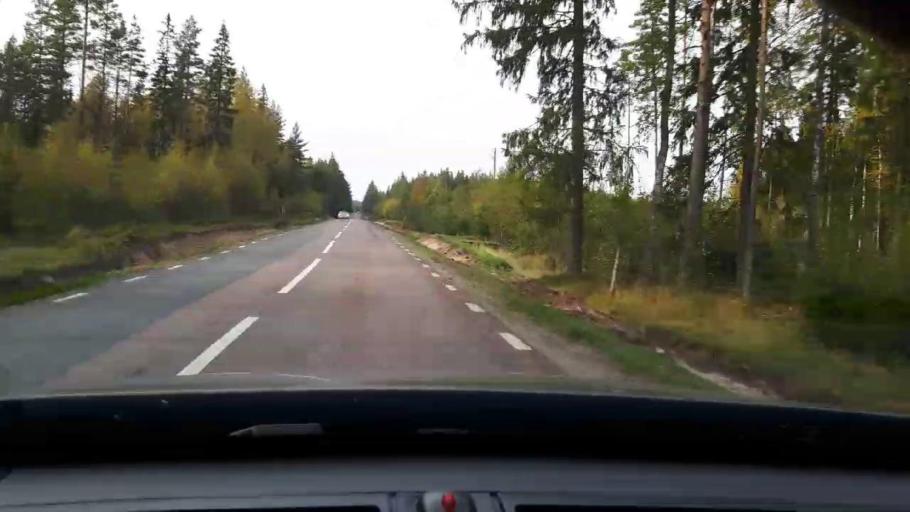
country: SE
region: Dalarna
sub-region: Gagnefs Kommun
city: Mockfjard
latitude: 60.3215
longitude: 14.9369
